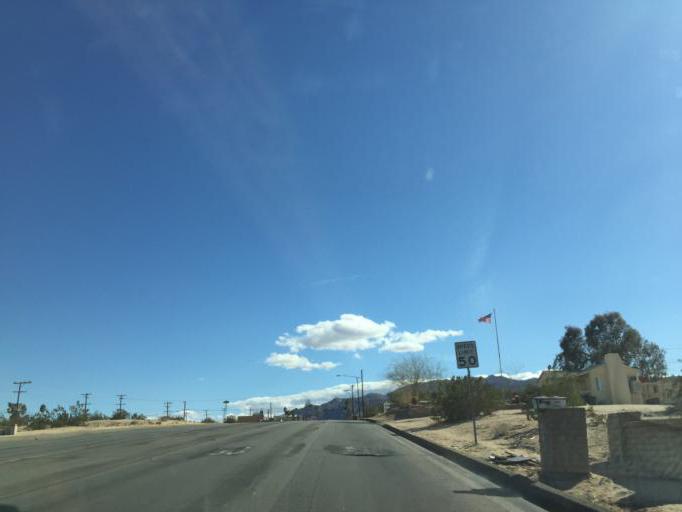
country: US
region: California
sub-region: San Bernardino County
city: Twentynine Palms
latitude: 34.1538
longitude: -116.0543
